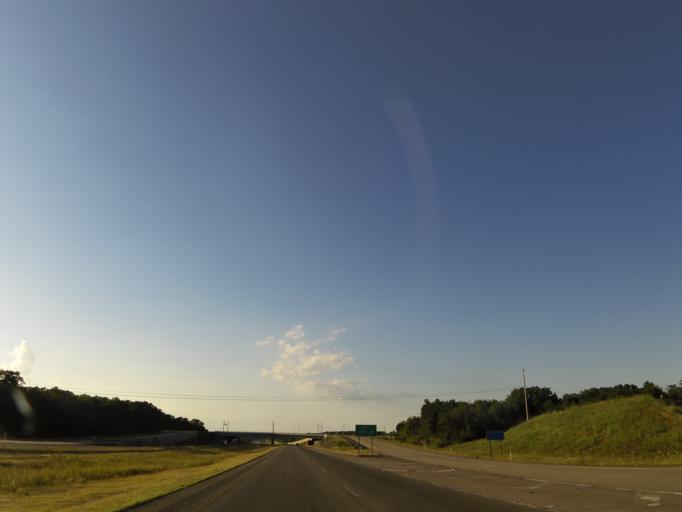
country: US
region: Tennessee
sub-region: Wilson County
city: Rural Hill
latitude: 36.0362
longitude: -86.4288
